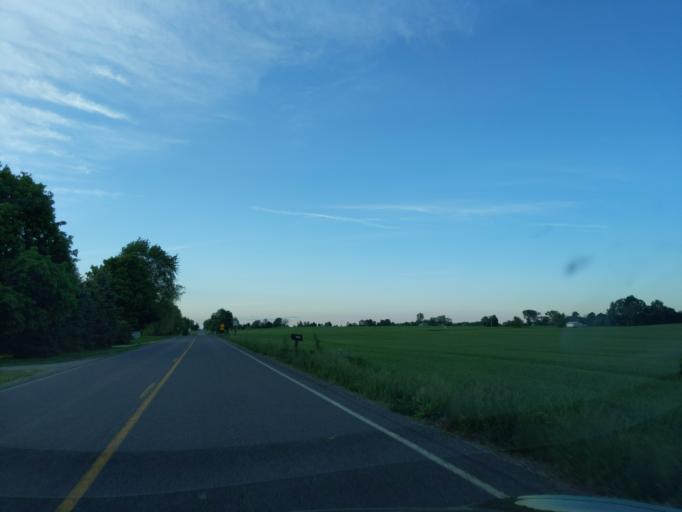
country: US
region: Michigan
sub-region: Ingham County
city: Williamston
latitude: 42.5743
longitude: -84.2984
